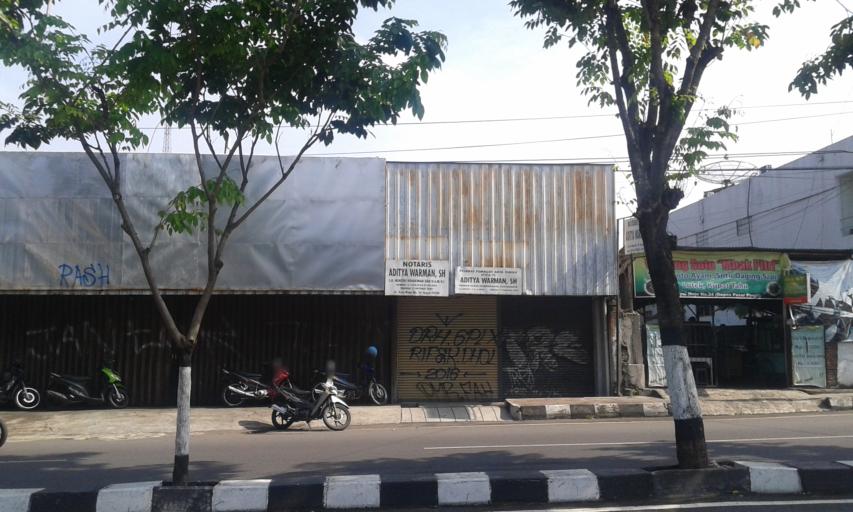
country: ID
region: Daerah Istimewa Yogyakarta
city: Yogyakarta
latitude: -7.7828
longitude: 110.3589
